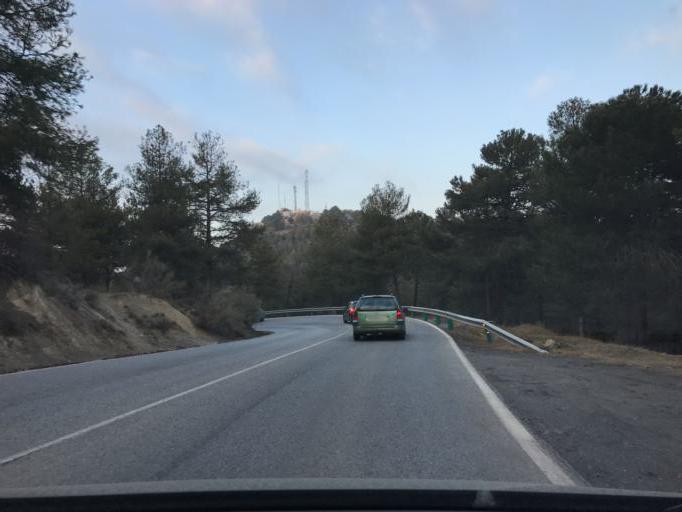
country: ES
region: Andalusia
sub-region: Provincia de Granada
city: Guejar-Sierra
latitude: 37.1388
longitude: -3.4608
